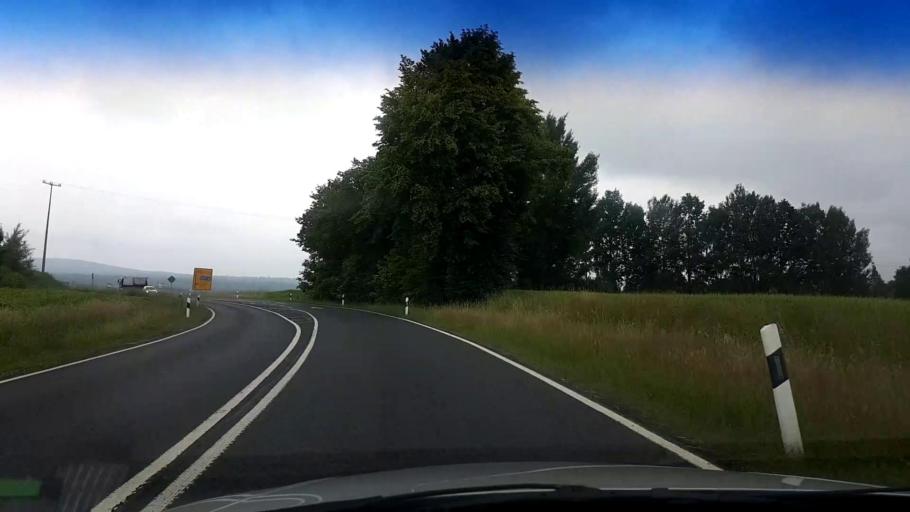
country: DE
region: Bavaria
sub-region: Upper Franconia
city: Hohenberg an der Eger
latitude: 50.0892
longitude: 12.2178
